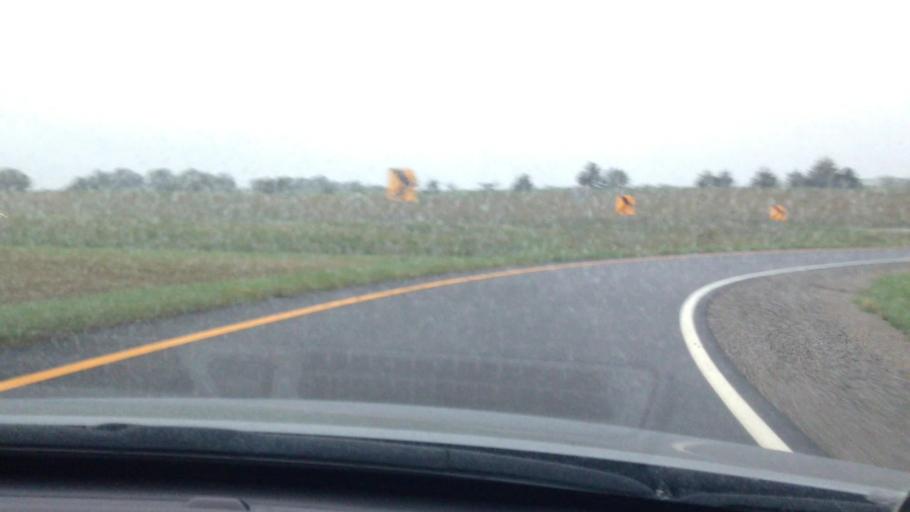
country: US
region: Kansas
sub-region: Brown County
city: Hiawatha
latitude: 39.8399
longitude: -95.5472
